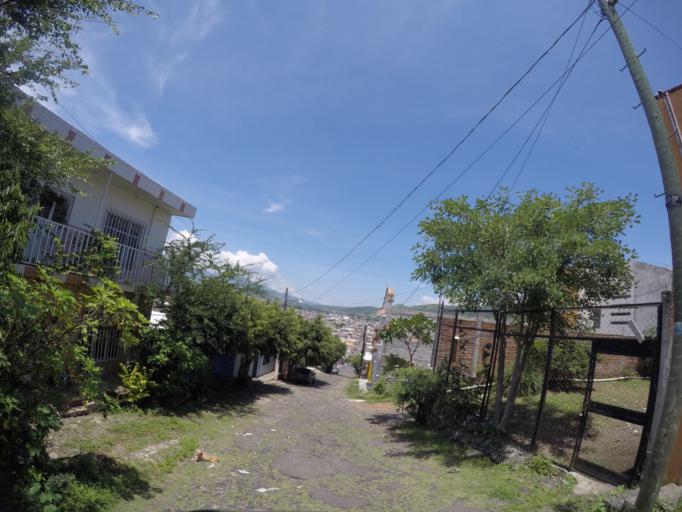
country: MX
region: Nayarit
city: Ixtlan del Rio
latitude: 21.0345
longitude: -104.3601
